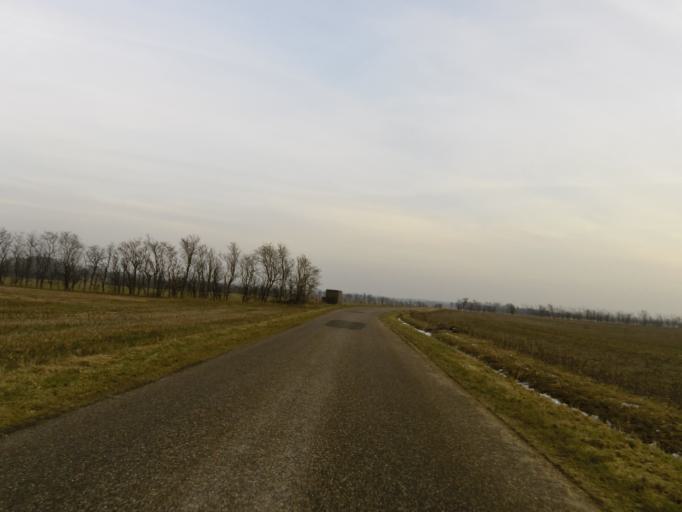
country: DK
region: South Denmark
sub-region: Haderslev Kommune
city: Gram
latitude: 55.3436
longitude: 8.9570
